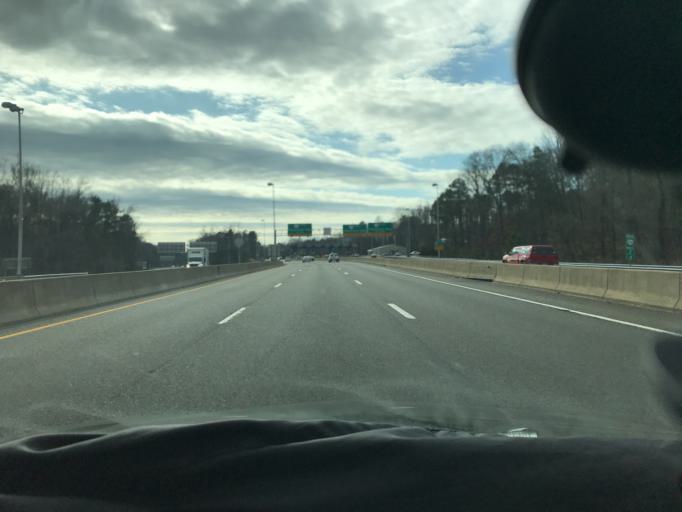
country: US
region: Virginia
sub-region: Chesterfield County
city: Bon Air
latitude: 37.5313
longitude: -77.5159
